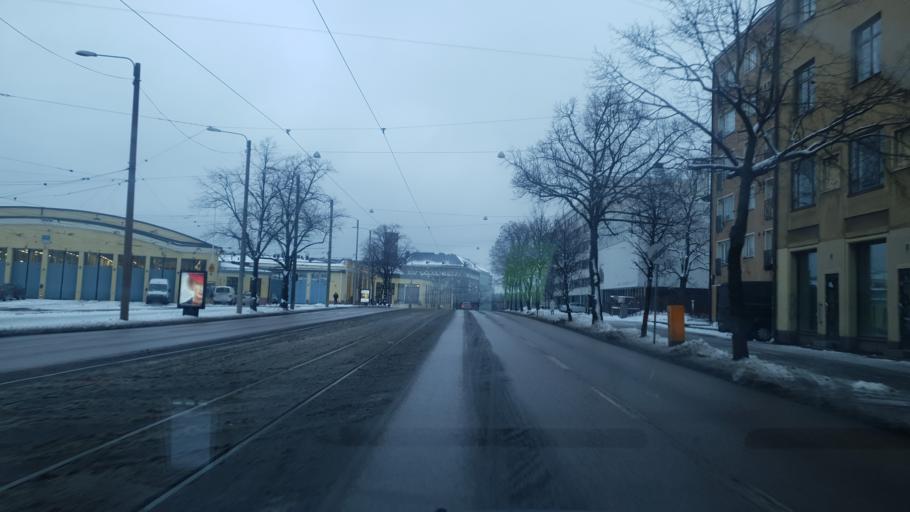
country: FI
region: Uusimaa
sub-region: Helsinki
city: Helsinki
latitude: 60.1938
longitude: 24.9643
